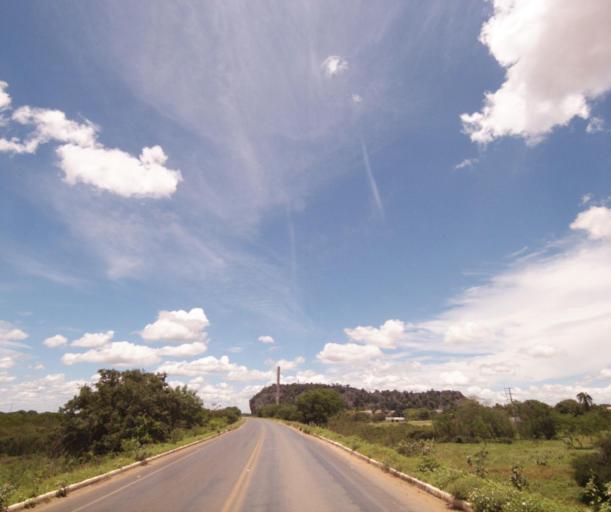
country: BR
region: Bahia
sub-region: Bom Jesus Da Lapa
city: Bom Jesus da Lapa
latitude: -13.2658
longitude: -43.4116
